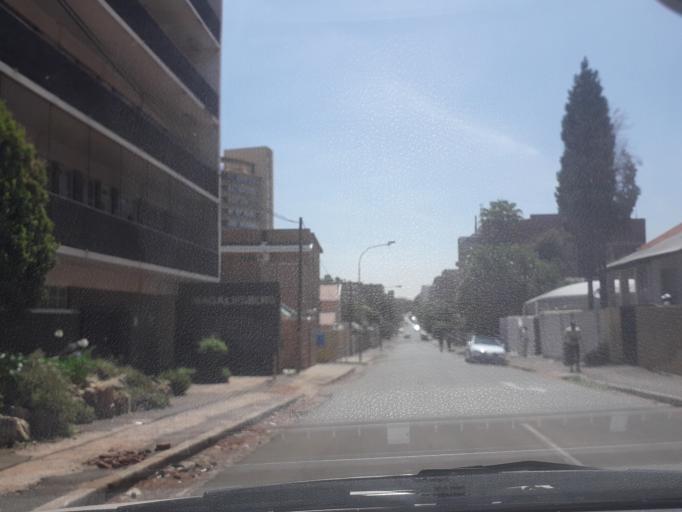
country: ZA
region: Gauteng
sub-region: City of Johannesburg Metropolitan Municipality
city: Johannesburg
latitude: -26.1817
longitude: 28.0513
